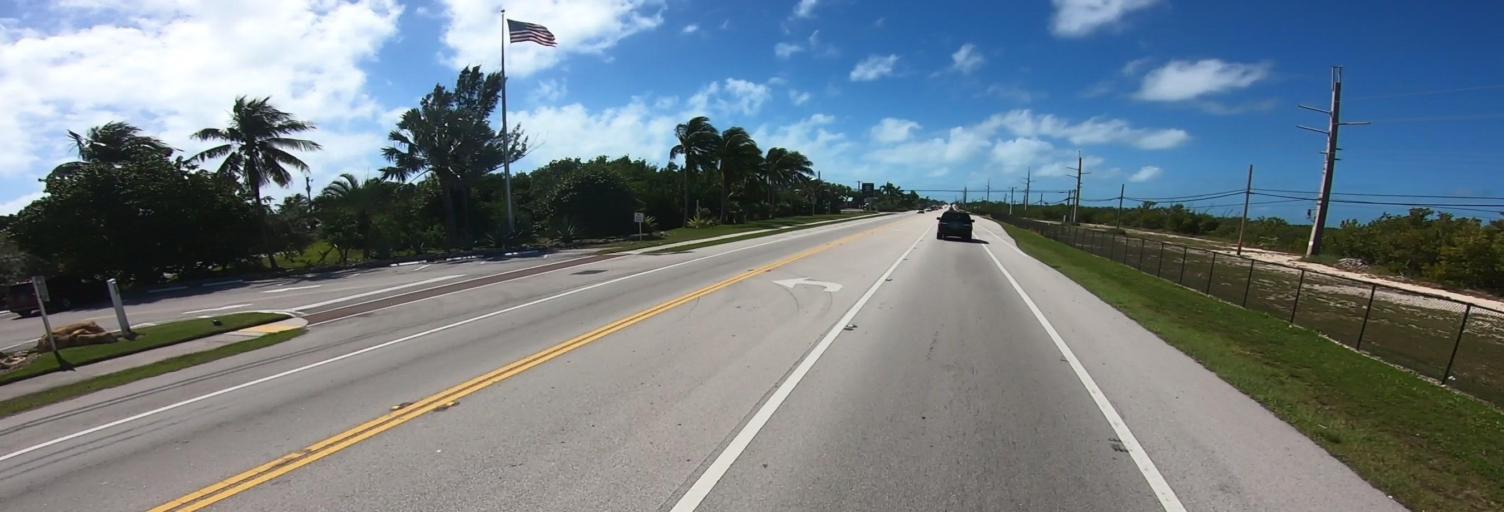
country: US
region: Florida
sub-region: Monroe County
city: Islamorada
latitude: 24.9444
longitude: -80.6049
